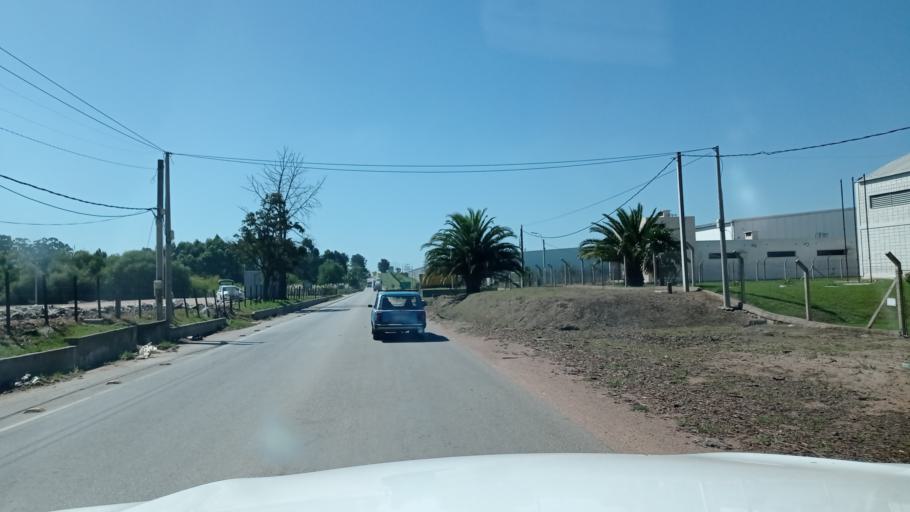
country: UY
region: Montevideo
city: Pajas Blancas
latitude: -34.8609
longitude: -56.2886
